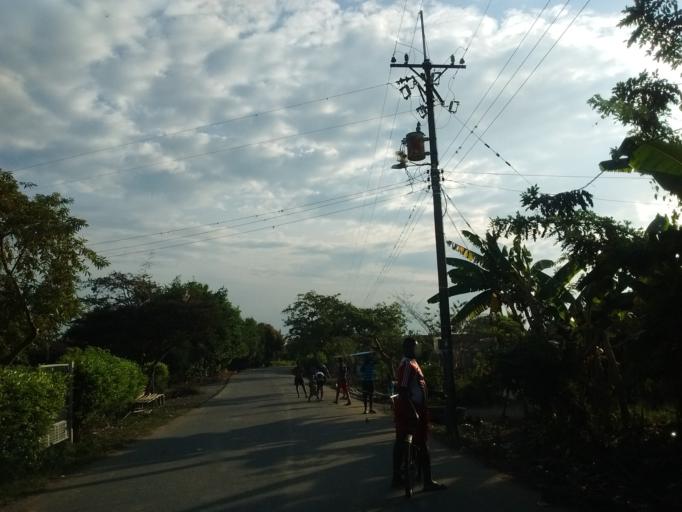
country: CO
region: Cauca
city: Puerto Tejada
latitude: 3.2201
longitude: -76.4489
